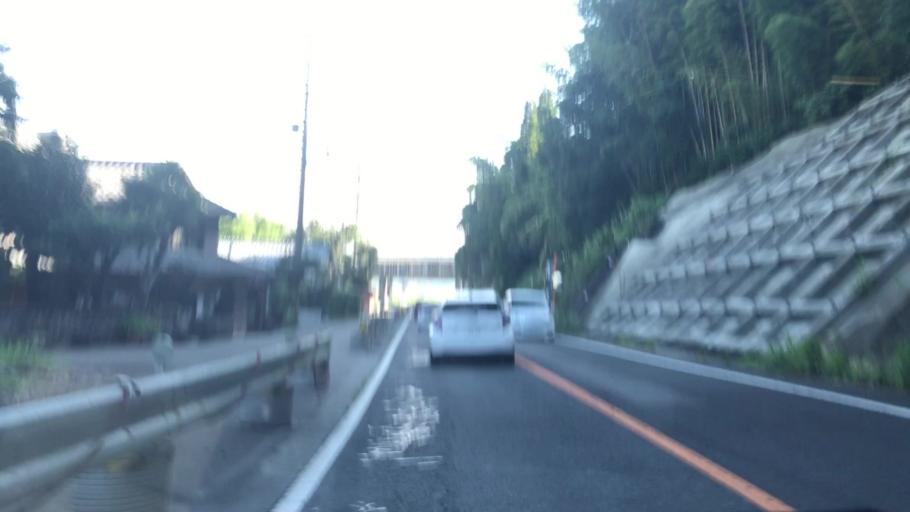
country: JP
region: Saga Prefecture
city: Takeocho-takeo
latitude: 33.2058
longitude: 130.0572
